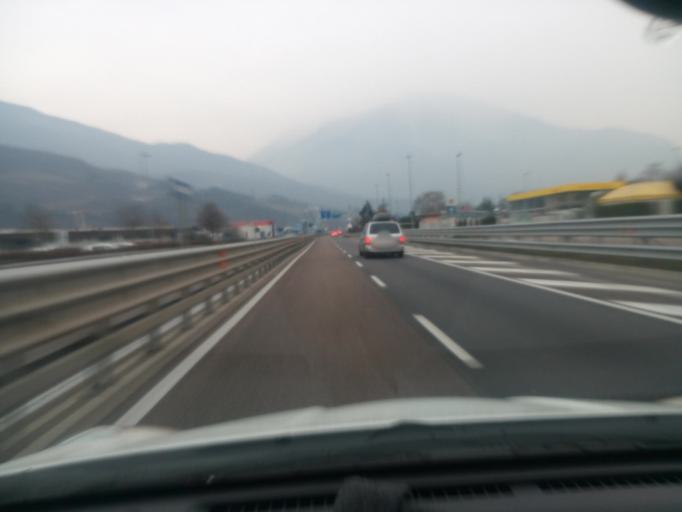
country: IT
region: Trentino-Alto Adige
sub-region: Provincia di Trento
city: Ravina
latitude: 46.0388
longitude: 11.1232
